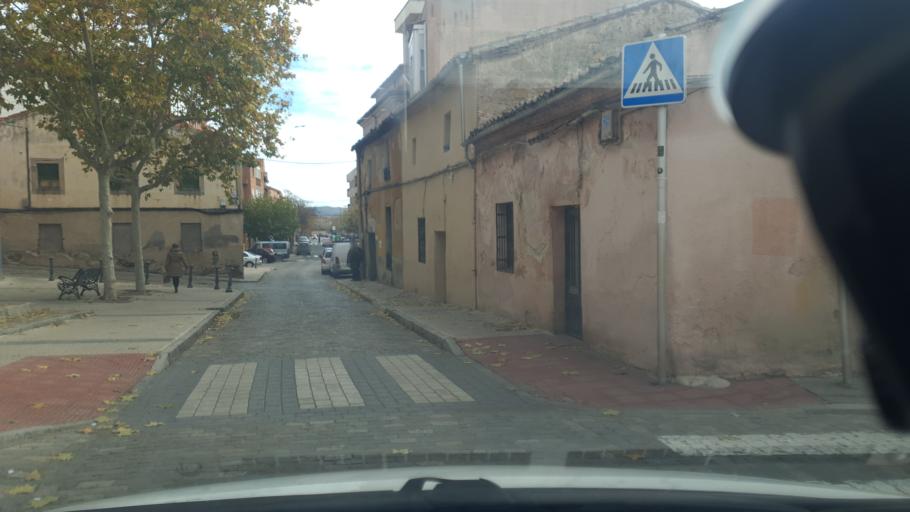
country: ES
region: Castille and Leon
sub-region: Provincia de Avila
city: Avila
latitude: 40.6521
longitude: -4.6947
